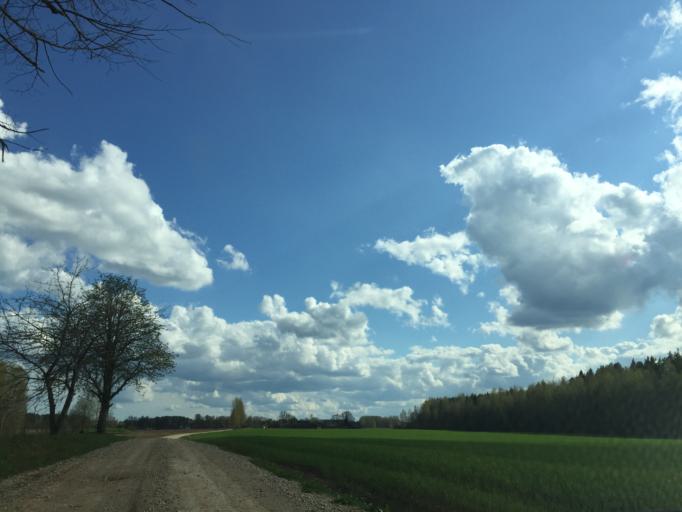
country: LV
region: Beverina
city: Murmuiza
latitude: 57.4273
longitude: 25.5494
